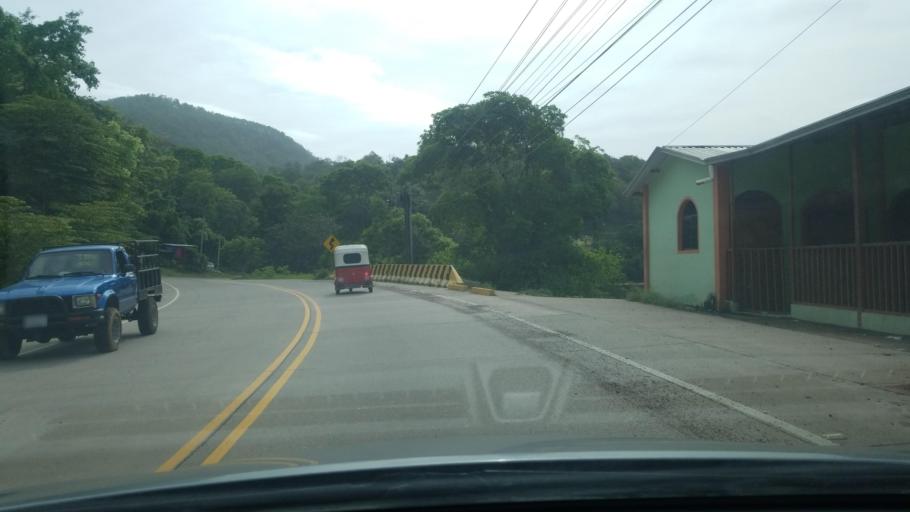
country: HN
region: Copan
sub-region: Santa Rita
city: Santa Rita, Copan
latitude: 14.8703
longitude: -89.0848
